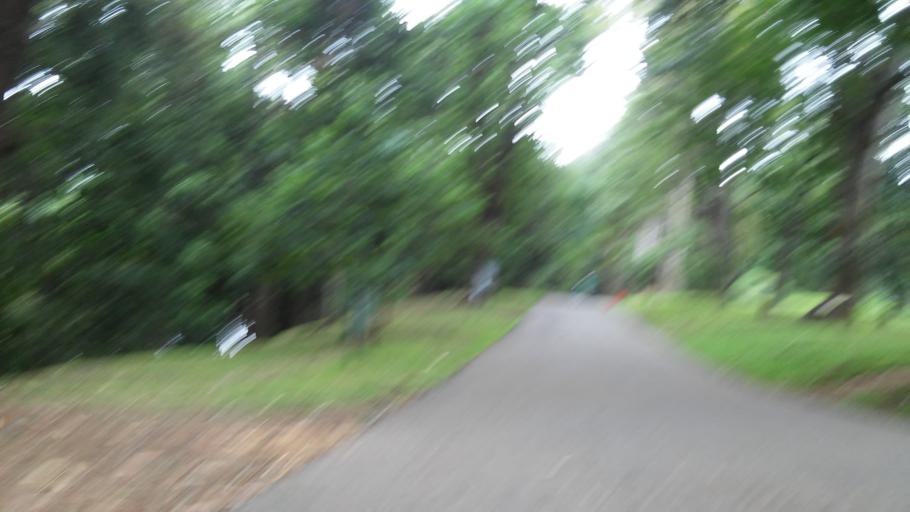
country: LK
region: Central
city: Kandy
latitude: 7.2715
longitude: 80.5938
